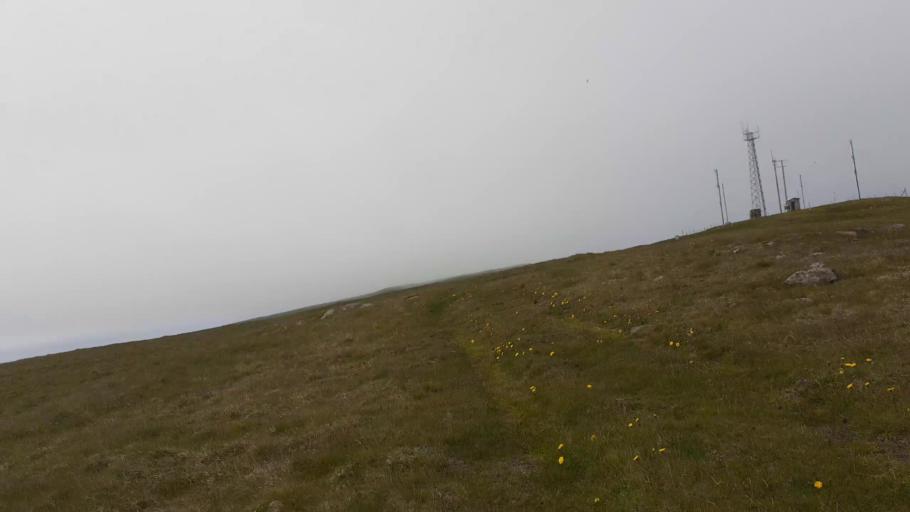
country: IS
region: Northeast
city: Dalvik
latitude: 66.5441
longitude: -17.9927
